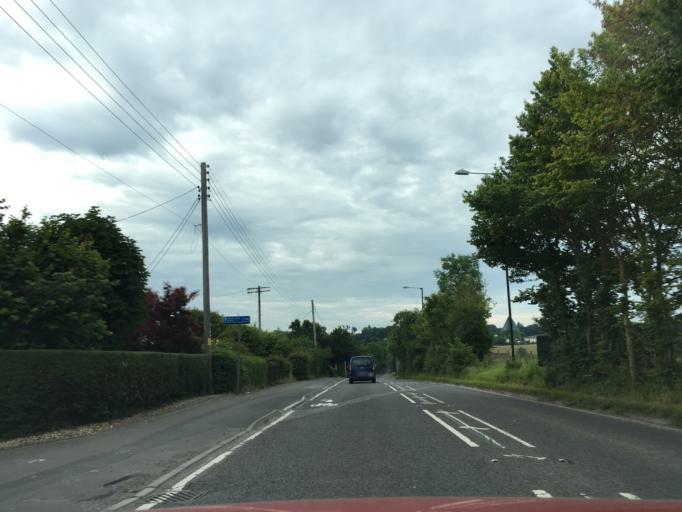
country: GB
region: England
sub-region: North Somerset
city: Easton-in-Gordano
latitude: 51.4683
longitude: -2.6748
